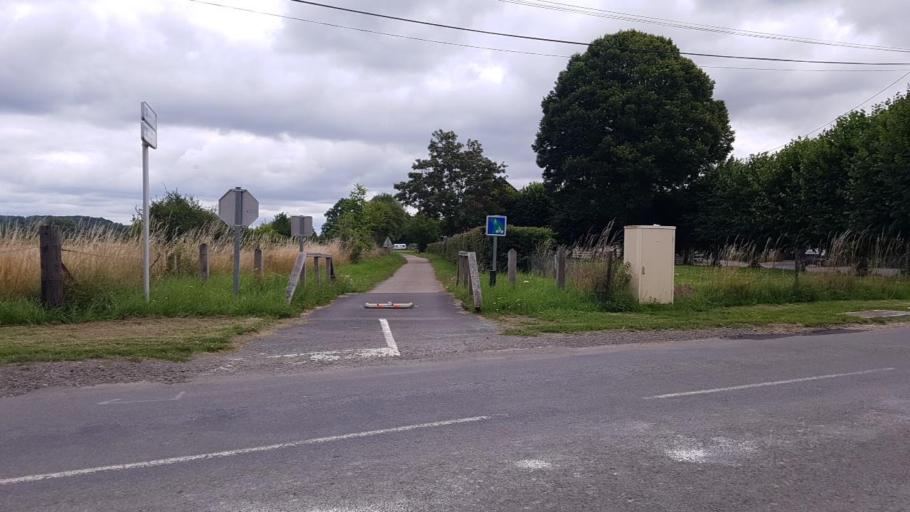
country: FR
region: Picardie
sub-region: Departement de l'Aisne
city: Buironfosse
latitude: 49.9065
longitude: 3.7811
